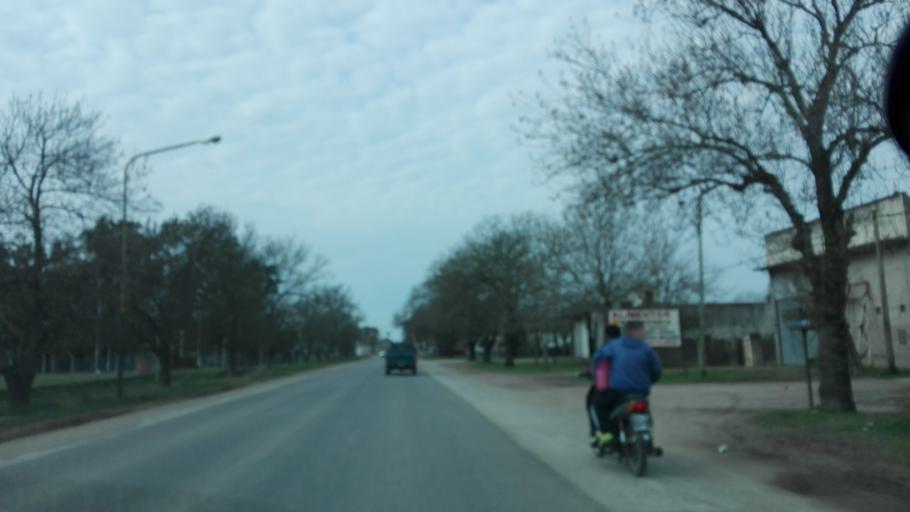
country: AR
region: Buenos Aires
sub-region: Partido de Chascomus
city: Chascomus
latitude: -35.5743
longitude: -57.9866
